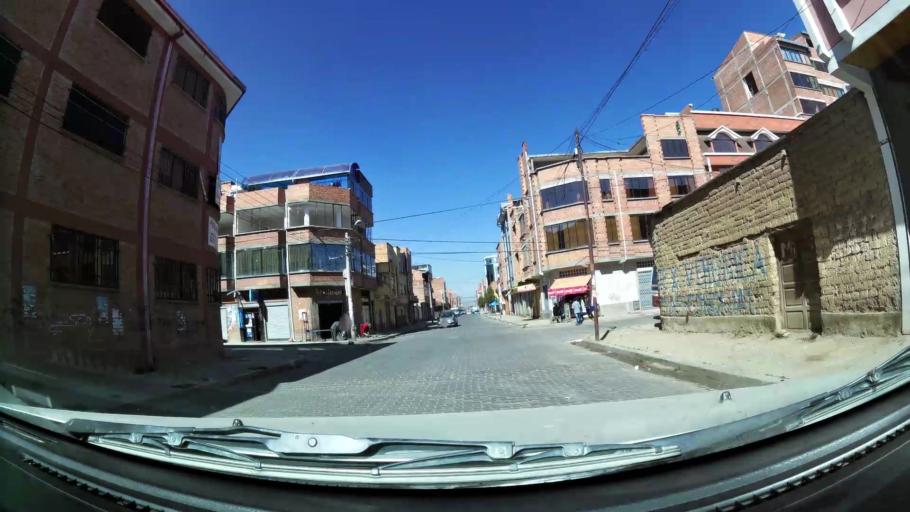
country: BO
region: La Paz
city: La Paz
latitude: -16.5192
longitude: -68.1555
